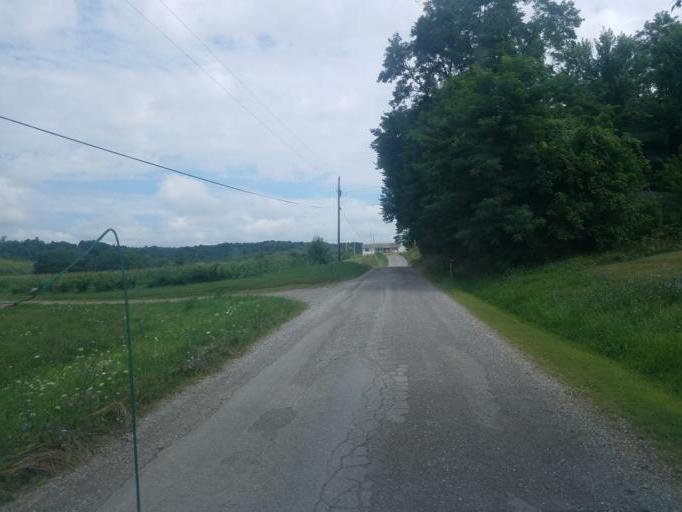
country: US
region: Ohio
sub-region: Belmont County
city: Barnesville
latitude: 40.0536
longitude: -81.3397
